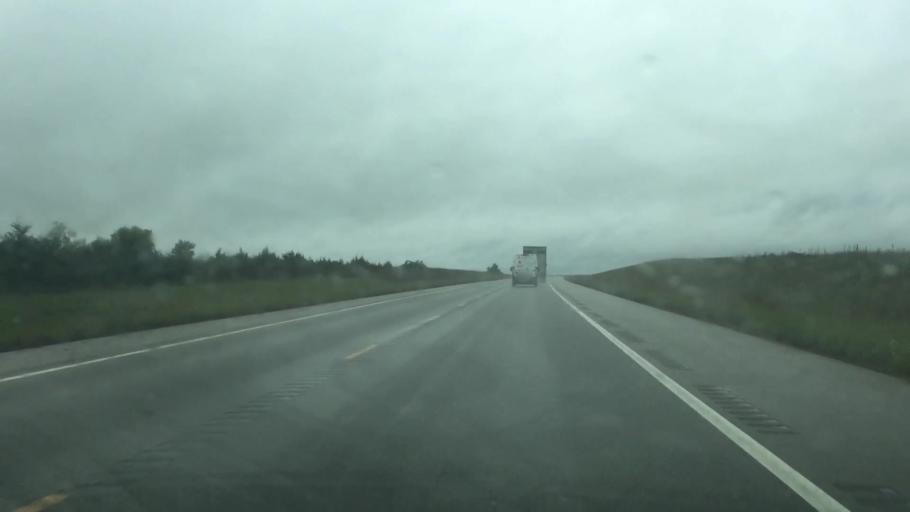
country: US
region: Kansas
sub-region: Allen County
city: Iola
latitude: 38.0914
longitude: -95.3626
